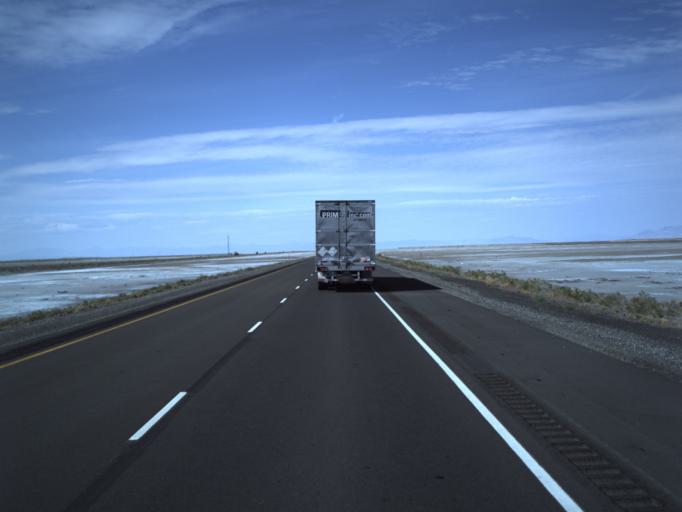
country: US
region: Utah
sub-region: Tooele County
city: Wendover
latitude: 40.7277
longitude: -113.2866
